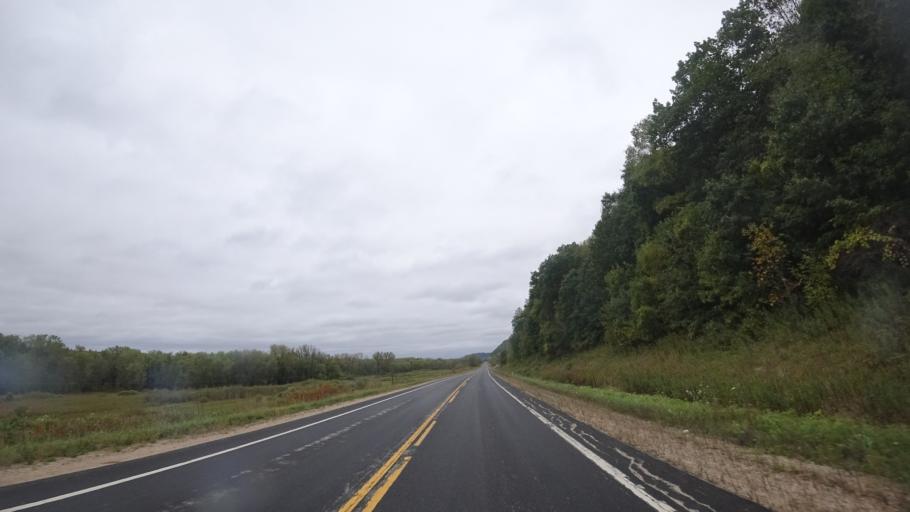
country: US
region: Wisconsin
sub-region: Grant County
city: Boscobel
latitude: 43.1936
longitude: -90.6593
